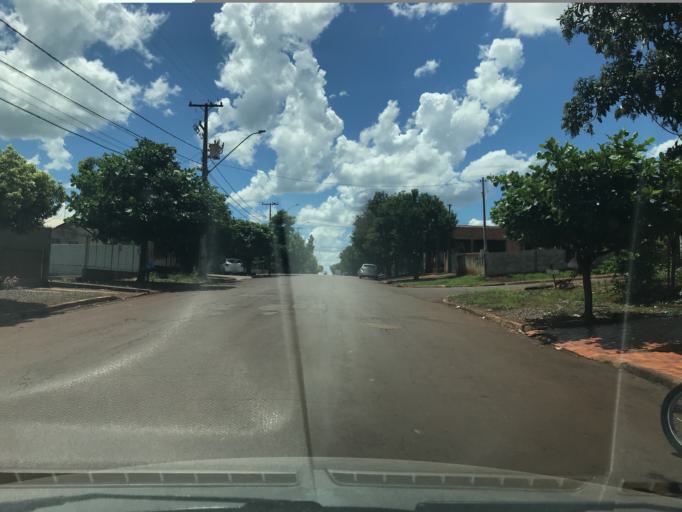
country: BR
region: Parana
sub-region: Palotina
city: Palotina
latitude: -24.2758
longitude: -53.8485
